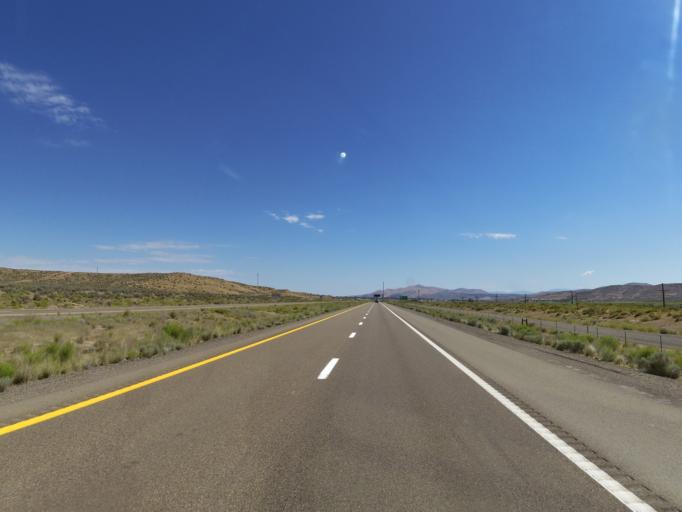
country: US
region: Nevada
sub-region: Elko County
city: Elko
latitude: 40.7981
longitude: -115.8413
